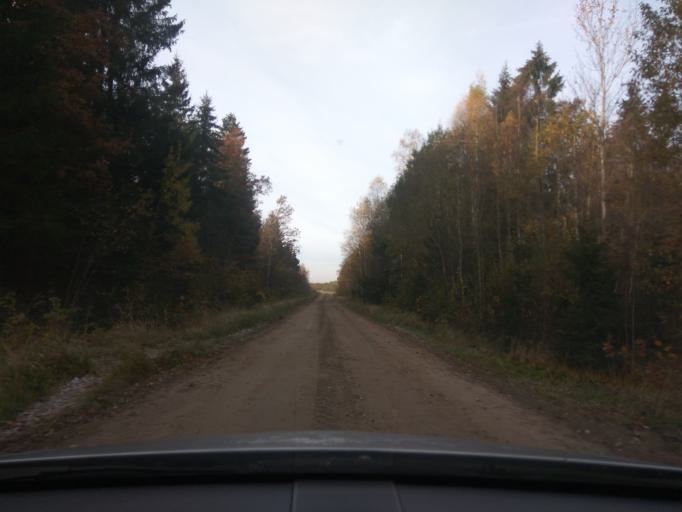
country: LV
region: Aizpute
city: Aizpute
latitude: 56.8412
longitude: 21.7175
